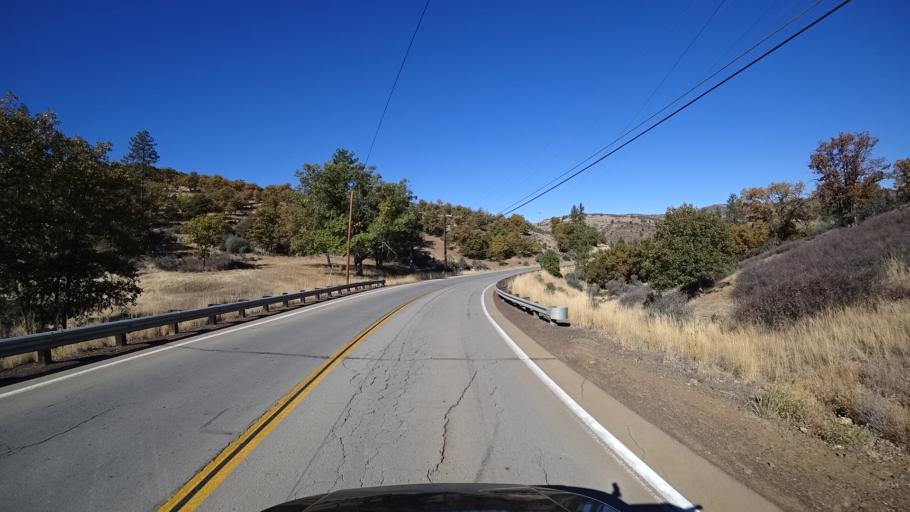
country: US
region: California
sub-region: Siskiyou County
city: Montague
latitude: 41.8948
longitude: -122.5060
